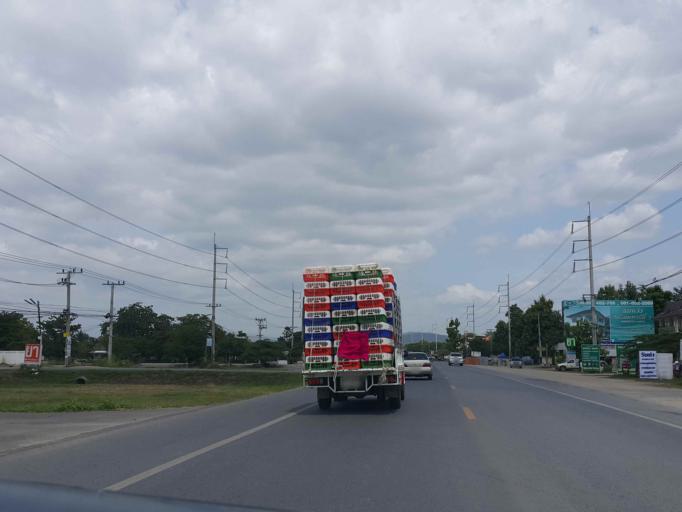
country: TH
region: Chiang Mai
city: Hang Dong
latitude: 18.7214
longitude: 98.9588
